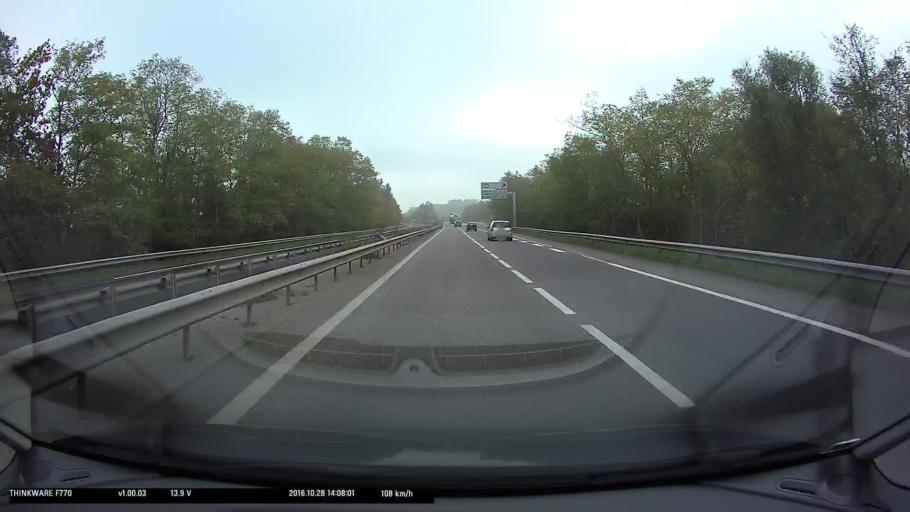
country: FR
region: Lorraine
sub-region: Departement de Meurthe-et-Moselle
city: Rosieres-aux-Salines
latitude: 48.6057
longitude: 6.3322
